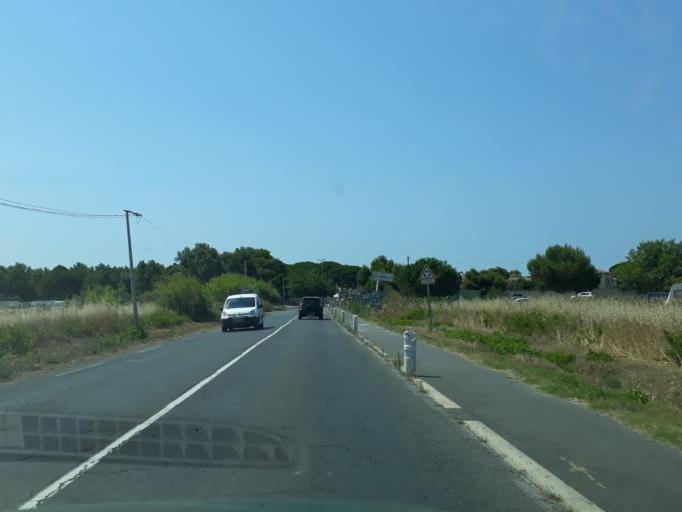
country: FR
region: Languedoc-Roussillon
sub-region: Departement de l'Herault
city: Agde
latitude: 43.2902
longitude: 3.4707
